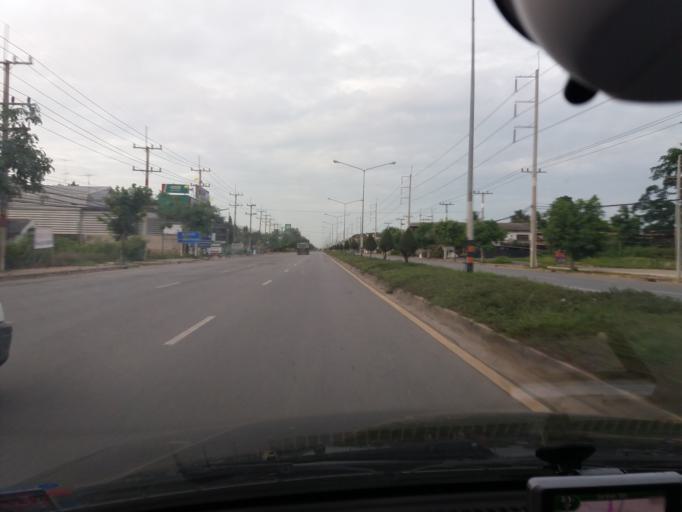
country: TH
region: Suphan Buri
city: U Thong
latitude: 14.3962
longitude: 99.8957
